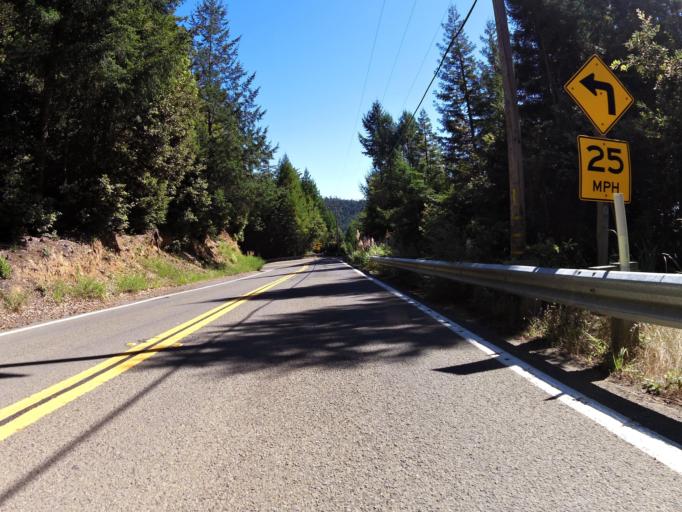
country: US
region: California
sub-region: Mendocino County
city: Fort Bragg
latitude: 39.7209
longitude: -123.8058
